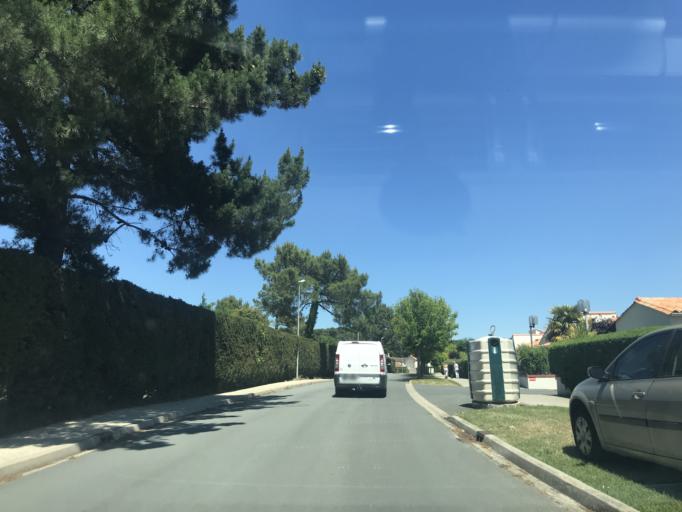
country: FR
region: Poitou-Charentes
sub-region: Departement de la Charente-Maritime
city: Saint-Palais-sur-Mer
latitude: 45.6500
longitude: -1.1090
